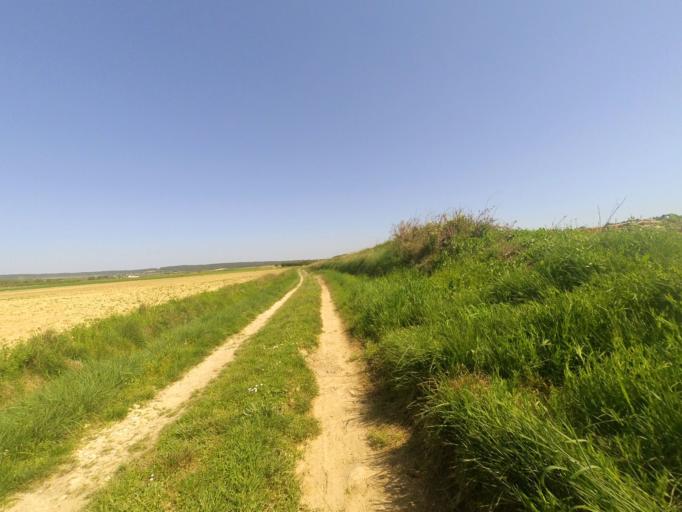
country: FR
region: Languedoc-Roussillon
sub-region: Departement du Gard
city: Congenies
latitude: 43.7658
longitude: 4.1869
